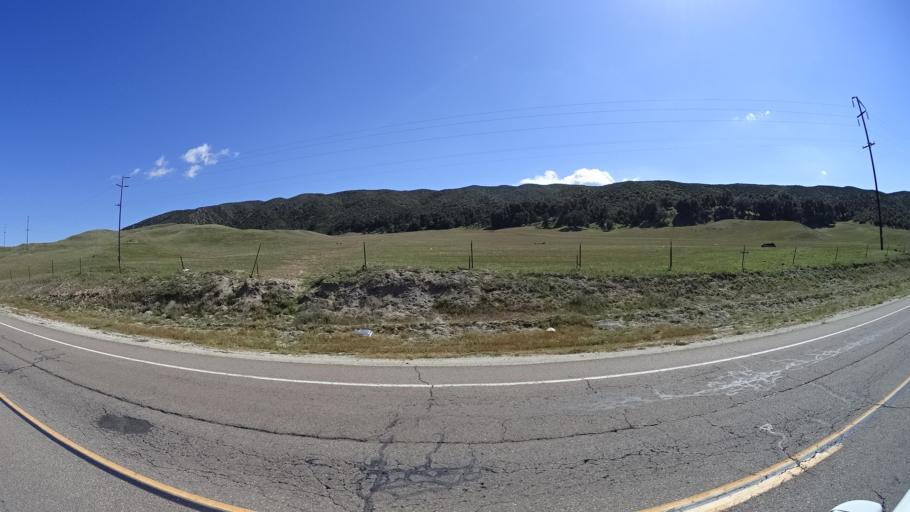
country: US
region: California
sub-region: San Diego County
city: Julian
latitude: 33.2319
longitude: -116.6375
